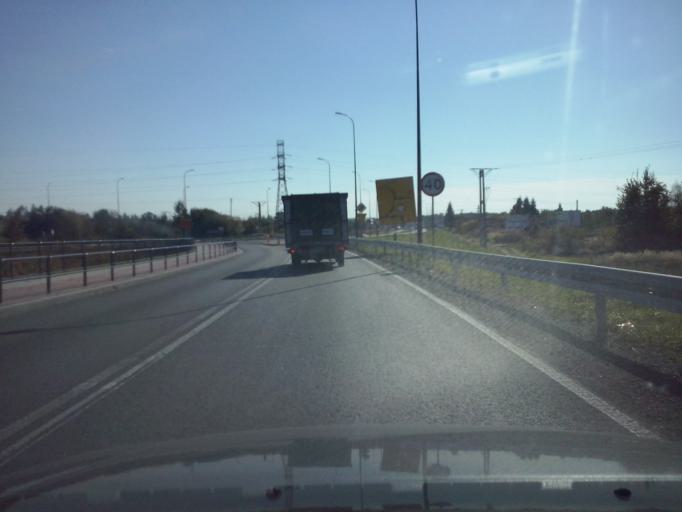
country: PL
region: Lublin Voivodeship
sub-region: Powiat bilgorajski
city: Bilgoraj
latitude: 50.5472
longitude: 22.7038
